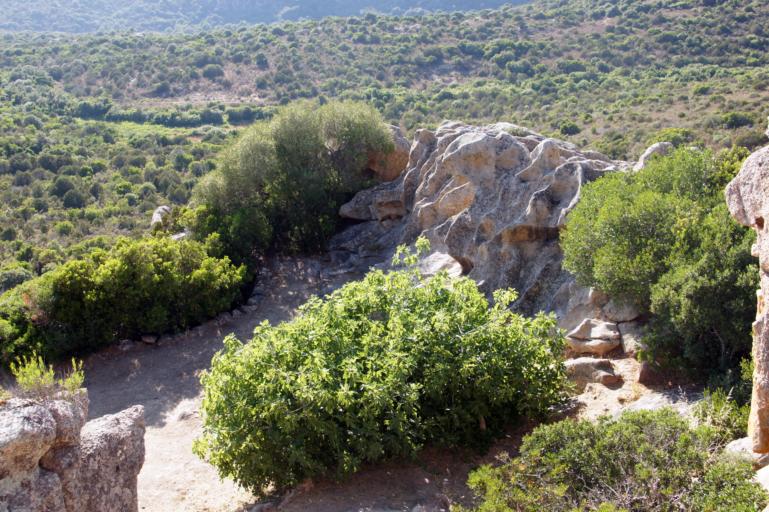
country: FR
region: Corsica
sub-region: Departement de la Corse-du-Sud
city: Sartene
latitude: 41.4991
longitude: 8.9486
